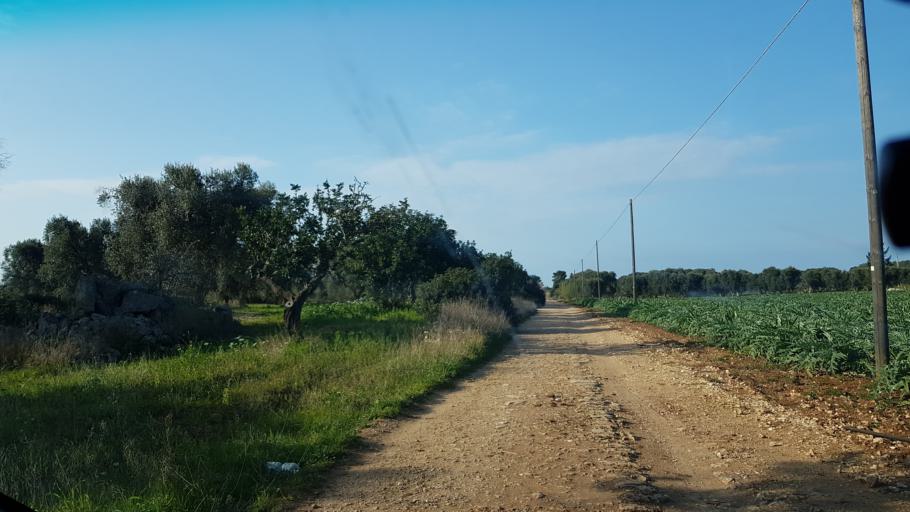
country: IT
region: Apulia
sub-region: Provincia di Brindisi
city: San Vito dei Normanni
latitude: 40.6760
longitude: 17.7899
